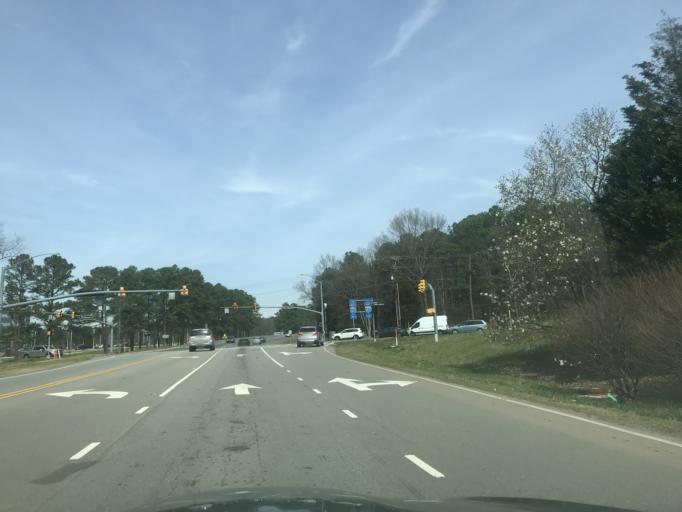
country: US
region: North Carolina
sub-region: Wake County
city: Morrisville
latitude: 35.8982
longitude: -78.8800
